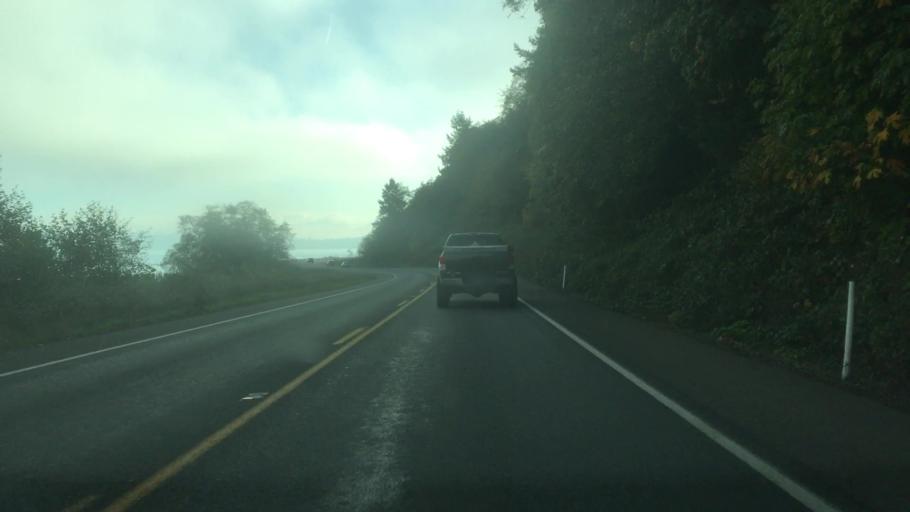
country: US
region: Oregon
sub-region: Clatsop County
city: Astoria
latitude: 46.2746
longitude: -123.8160
